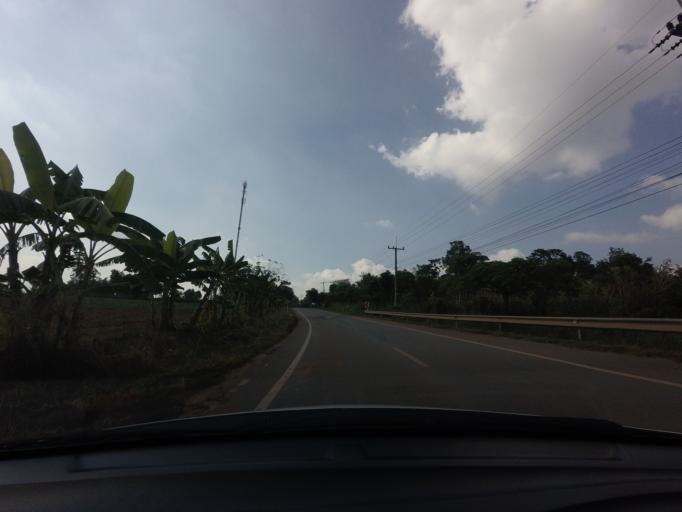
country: TH
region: Nakhon Ratchasima
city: Wang Nam Khiao
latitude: 14.4578
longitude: 101.6638
